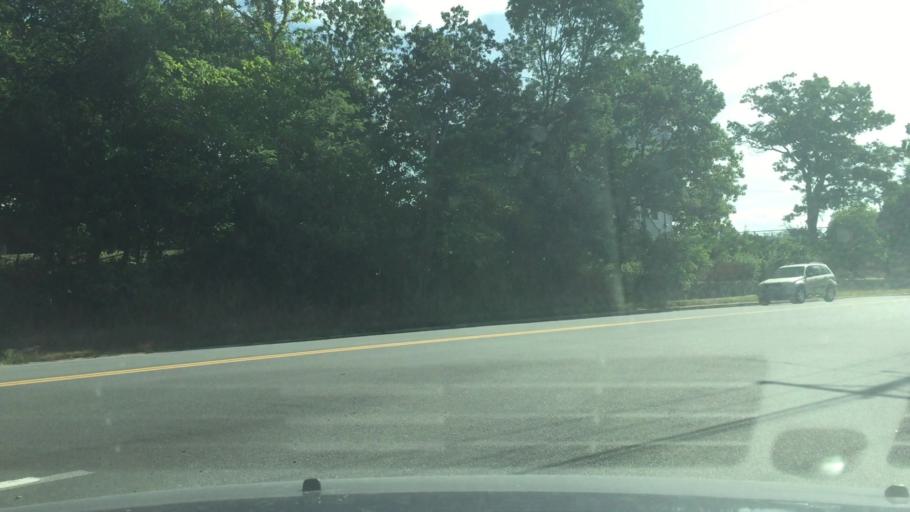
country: US
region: Massachusetts
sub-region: Essex County
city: North Andover
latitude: 42.6970
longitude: -71.1409
